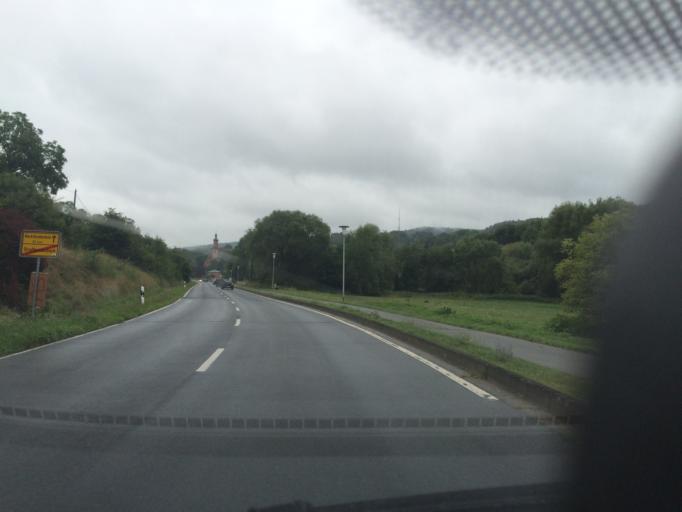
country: DE
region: Bavaria
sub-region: Regierungsbezirk Unterfranken
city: Haibach
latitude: 49.9581
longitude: 9.2484
